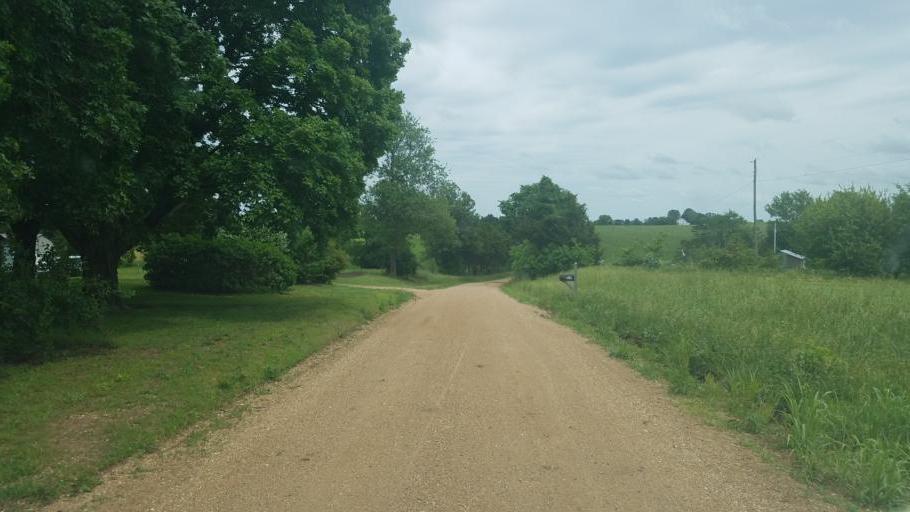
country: US
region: Missouri
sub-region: Moniteau County
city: Tipton
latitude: 38.5516
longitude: -92.7329
